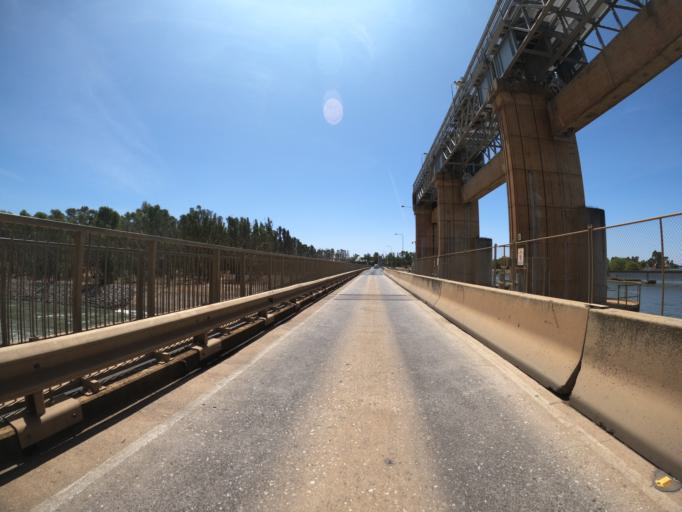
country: AU
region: Victoria
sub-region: Moira
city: Yarrawonga
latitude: -36.0094
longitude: 145.9995
